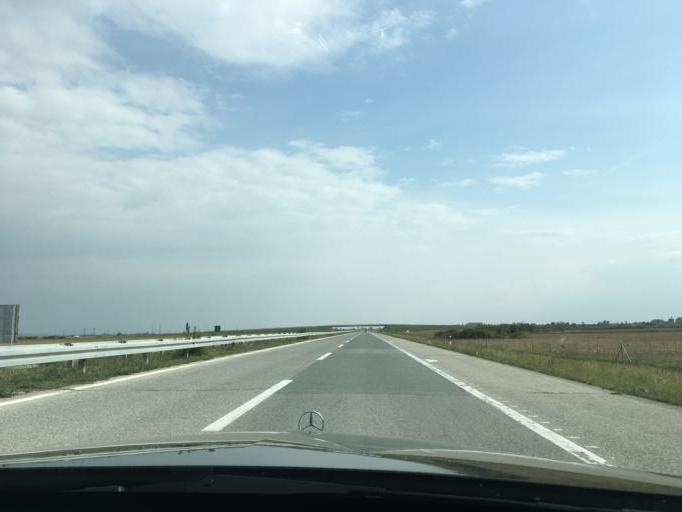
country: RS
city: Macvanska Mitrovica
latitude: 45.0180
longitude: 19.5361
